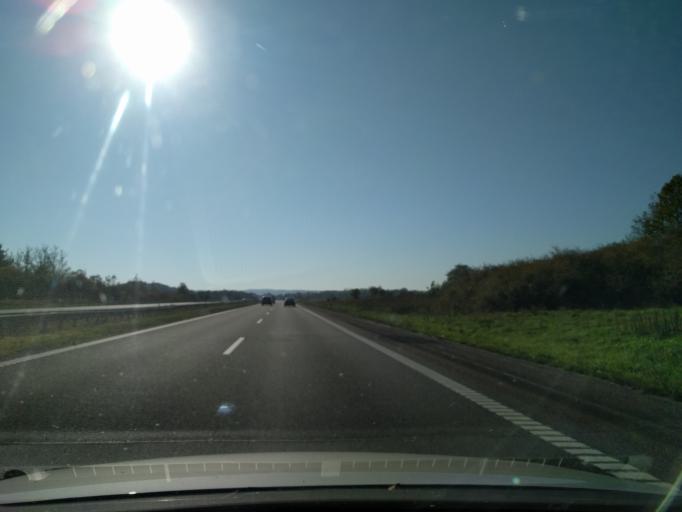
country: DK
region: Zealand
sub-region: Faxe Kommune
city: Ronnede
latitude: 55.2888
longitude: 12.0178
